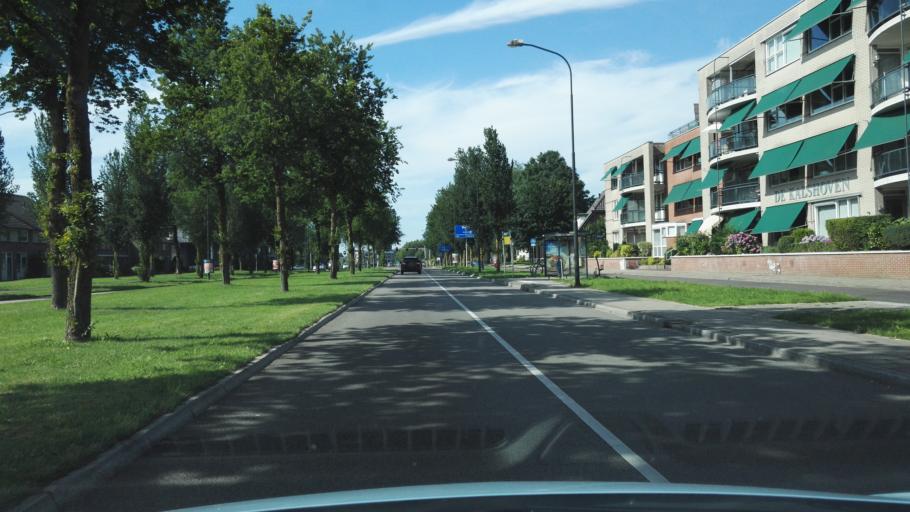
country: NL
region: Gelderland
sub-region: Gemeente Apeldoorn
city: Apeldoorn
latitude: 52.2030
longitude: 5.9589
